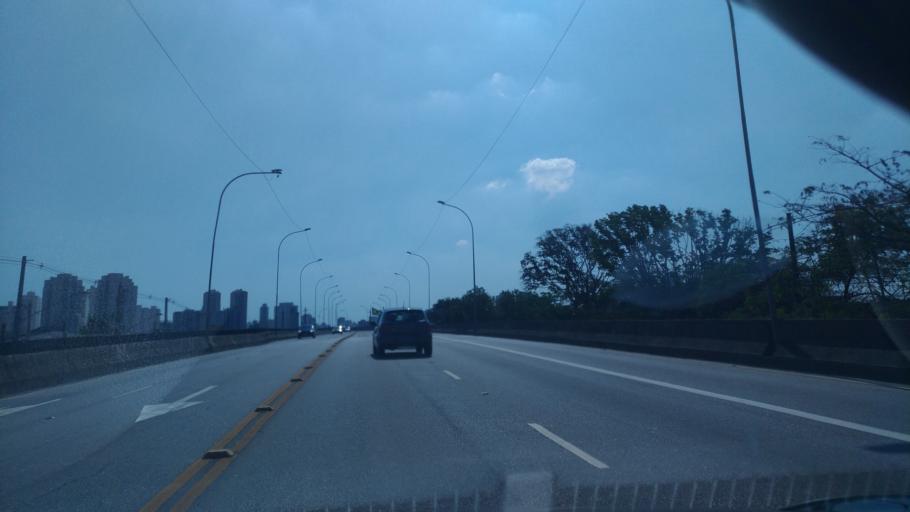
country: BR
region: Sao Paulo
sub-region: Sao Paulo
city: Sao Paulo
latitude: -23.5818
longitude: -46.5942
